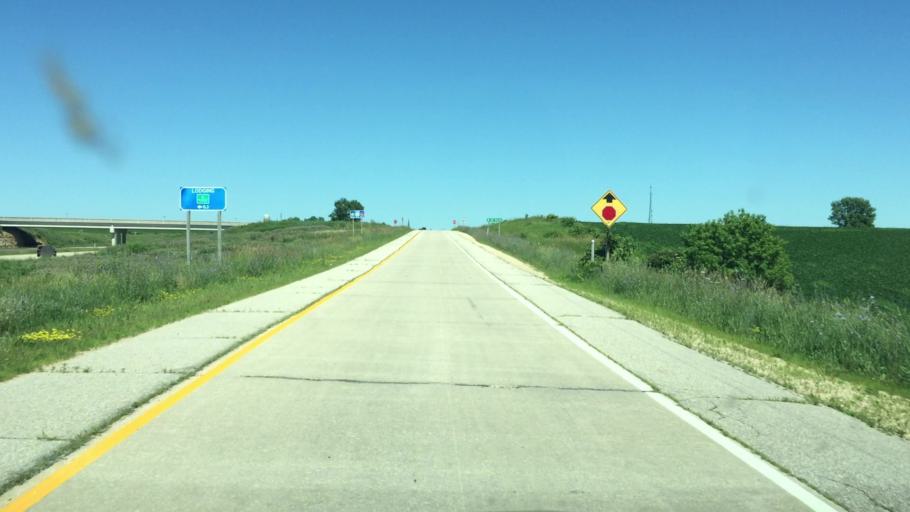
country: US
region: Wisconsin
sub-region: Dane County
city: Mount Horeb
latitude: 43.0032
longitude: -89.7053
